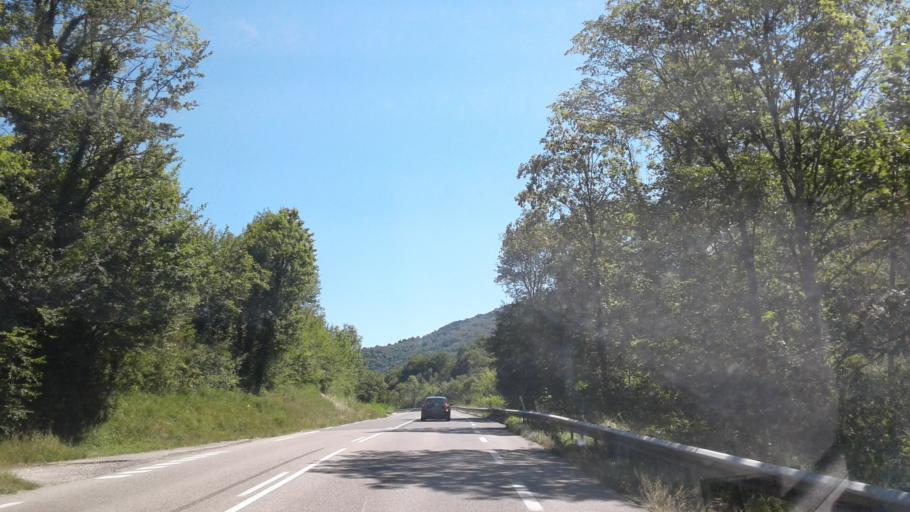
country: FR
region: Rhone-Alpes
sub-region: Departement de l'Ain
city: Tenay
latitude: 45.9406
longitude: 5.4828
